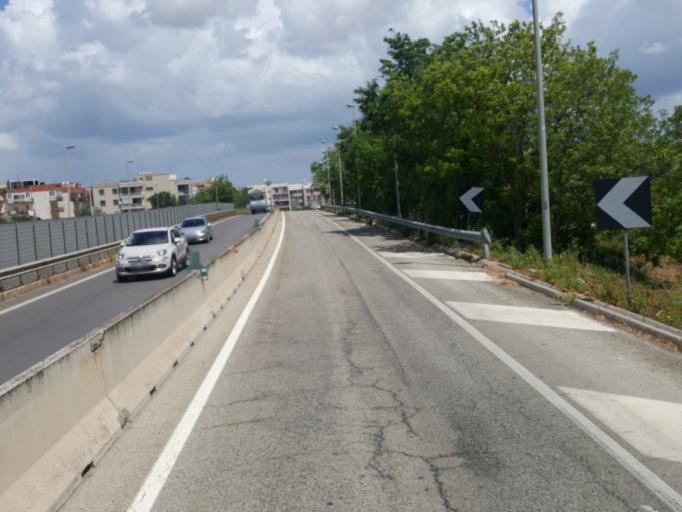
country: IT
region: Apulia
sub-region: Provincia di Bari
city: Modugno
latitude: 41.0852
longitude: 16.7729
